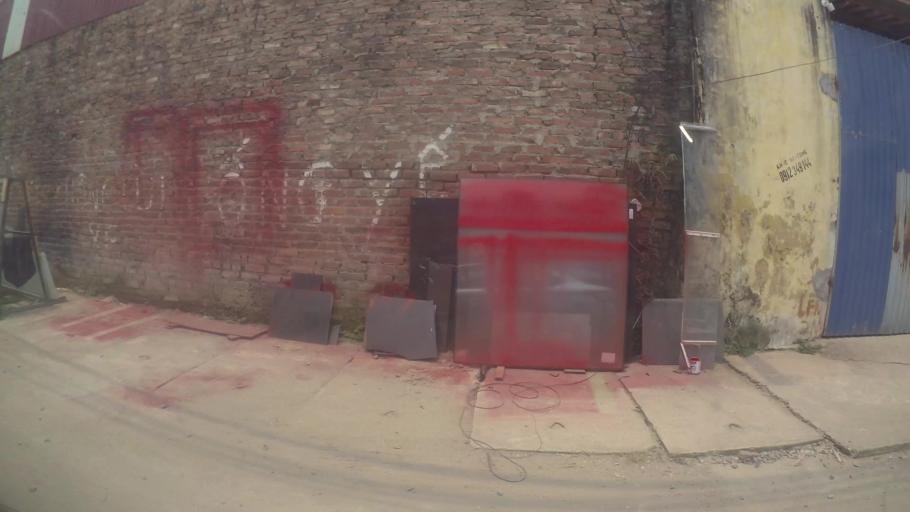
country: VN
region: Ha Noi
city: Ha Dong
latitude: 20.9922
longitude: 105.7400
